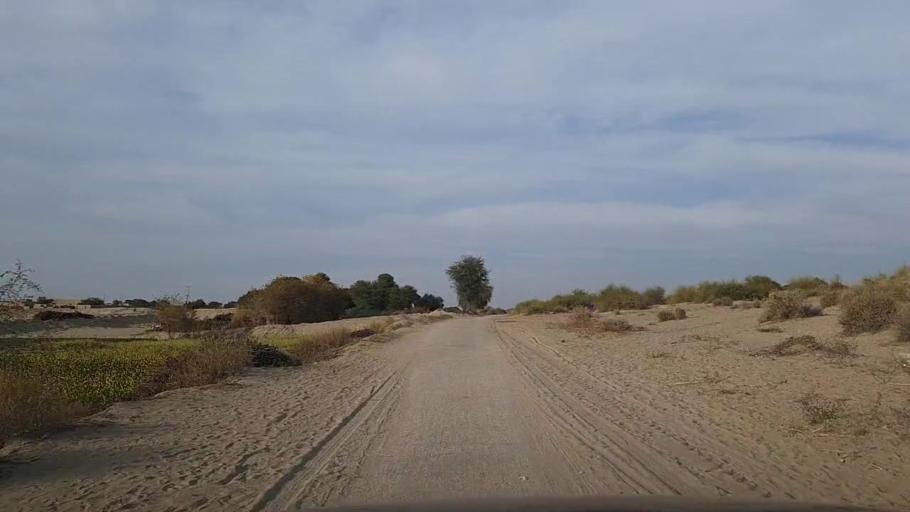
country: PK
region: Sindh
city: Jam Sahib
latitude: 26.4572
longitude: 68.5700
